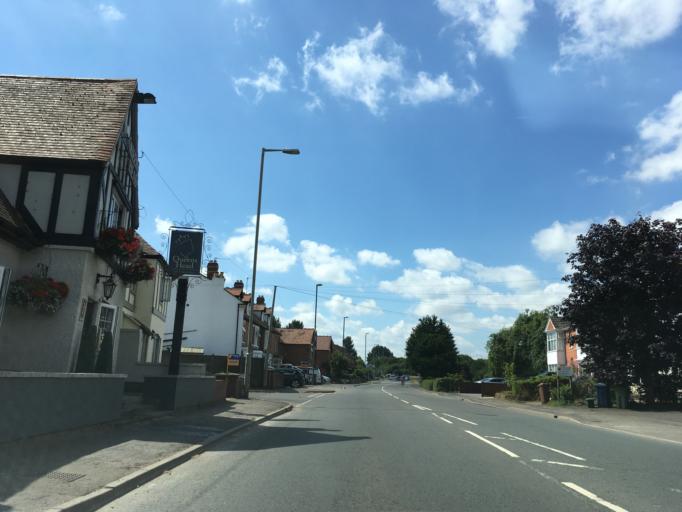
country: GB
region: England
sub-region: Gloucestershire
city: Gloucester
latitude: 51.8849
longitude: -2.2365
